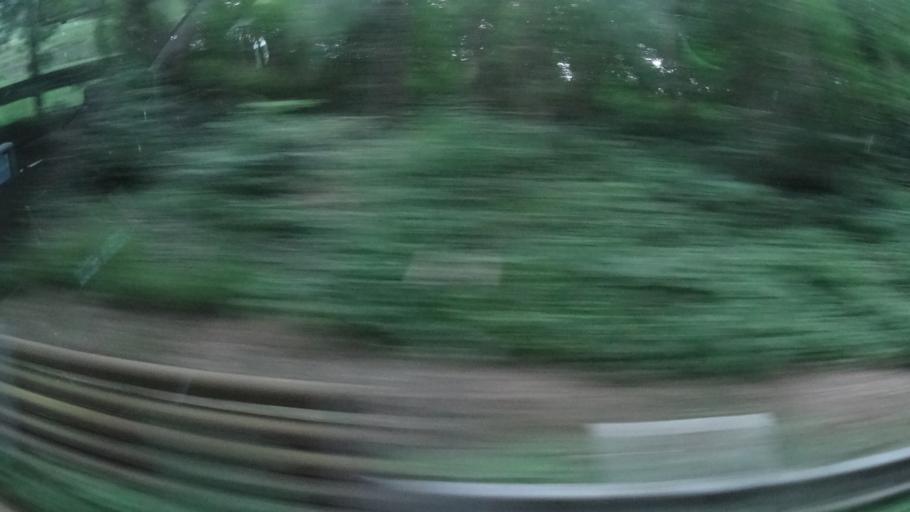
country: DE
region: Lower Saxony
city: Pegestorf
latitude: 51.9134
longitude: 9.4670
